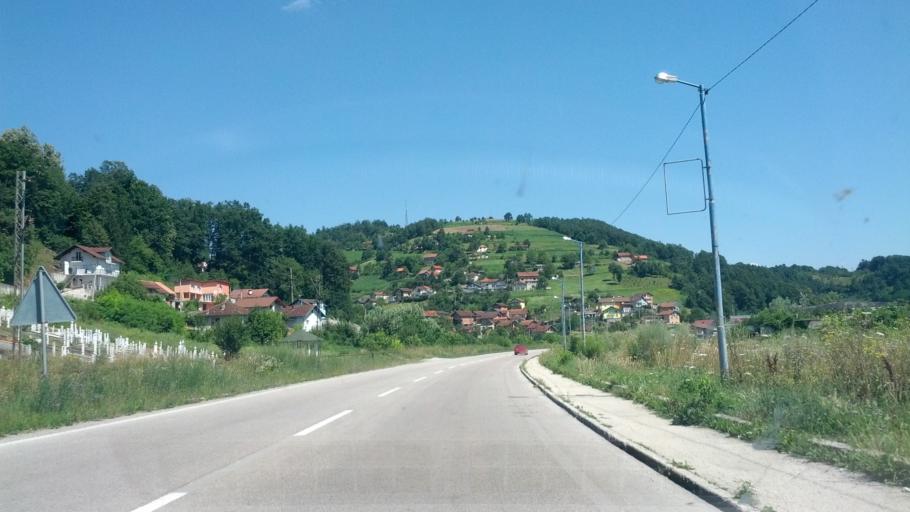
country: BA
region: Federation of Bosnia and Herzegovina
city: Bosanska Krupa
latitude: 44.8920
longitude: 16.1540
